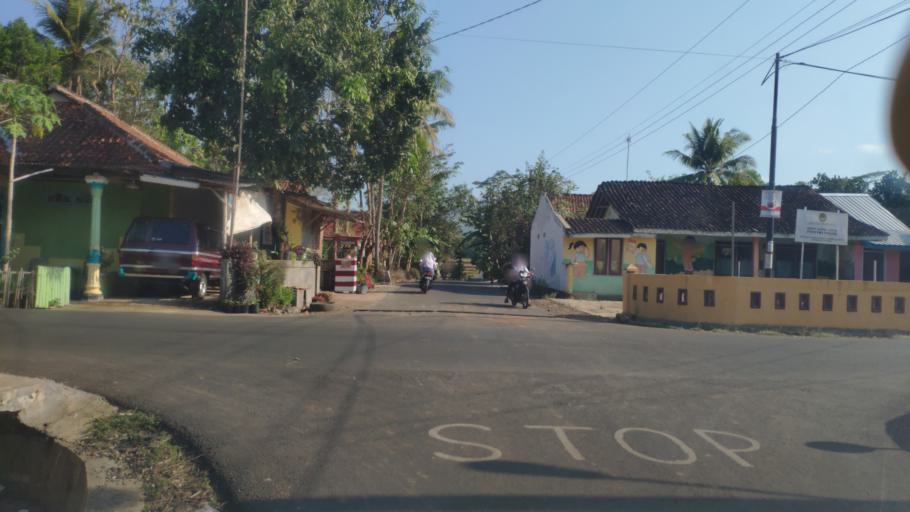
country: ID
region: Central Java
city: Purbalingga
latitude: -7.4769
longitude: 109.4619
